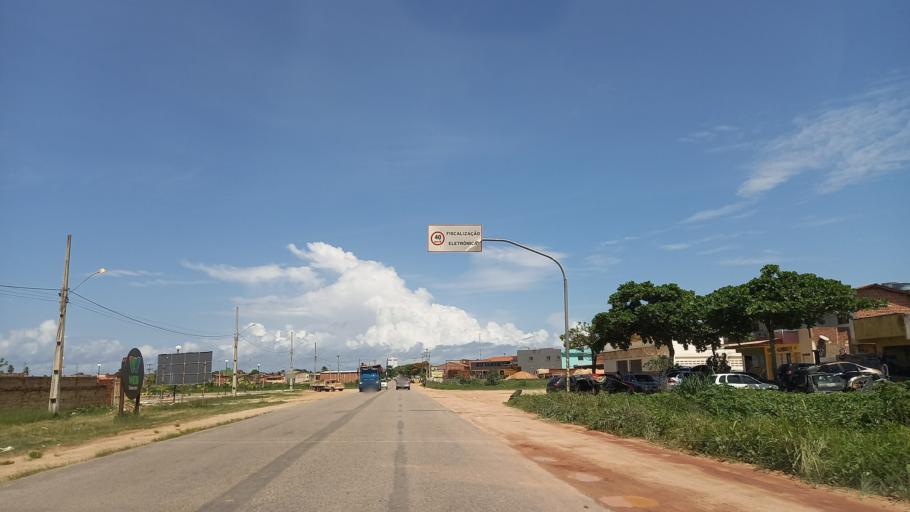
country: BR
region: Pernambuco
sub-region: Sao Jose Da Coroa Grande
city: Sao Jose da Coroa Grande
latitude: -8.8863
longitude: -35.1536
